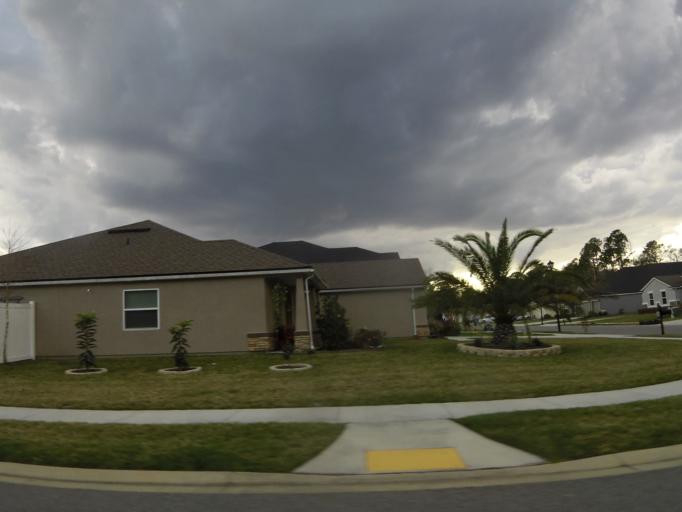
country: US
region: Florida
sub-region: Saint Johns County
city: Fruit Cove
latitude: 30.1718
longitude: -81.5659
